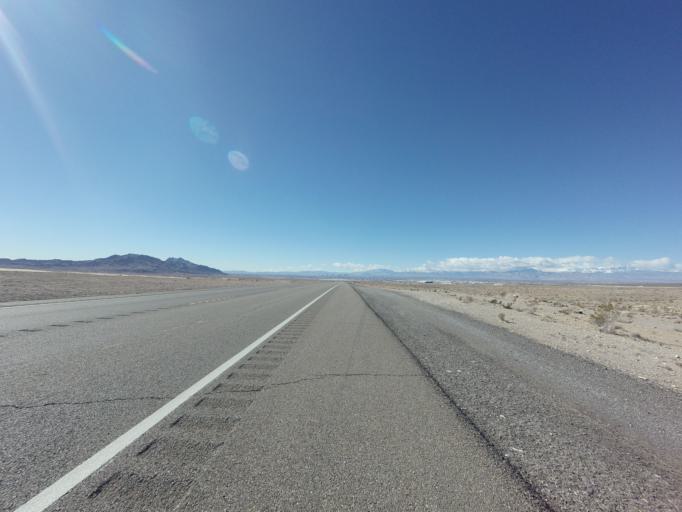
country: US
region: Nevada
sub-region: Clark County
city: Nellis Air Force Base
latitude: 36.2973
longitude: -114.9620
